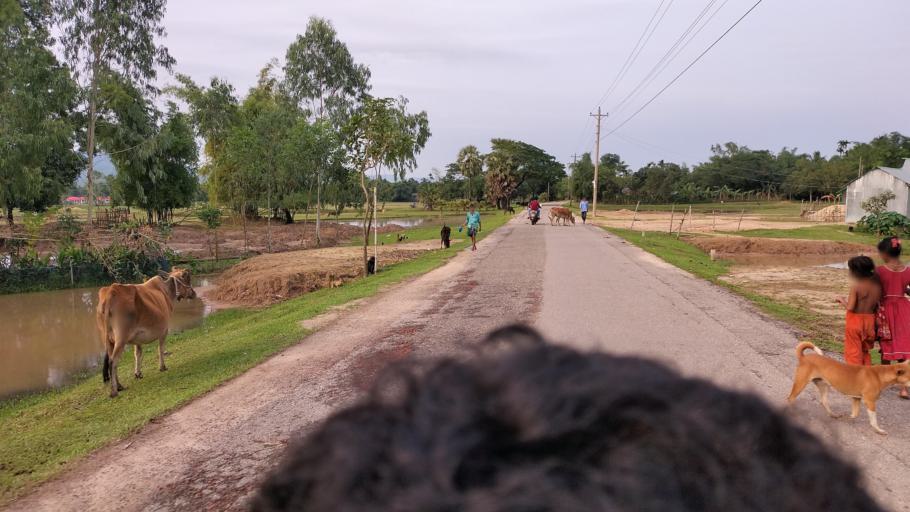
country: BD
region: Dhaka
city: Netrakona
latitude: 25.1353
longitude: 90.9165
